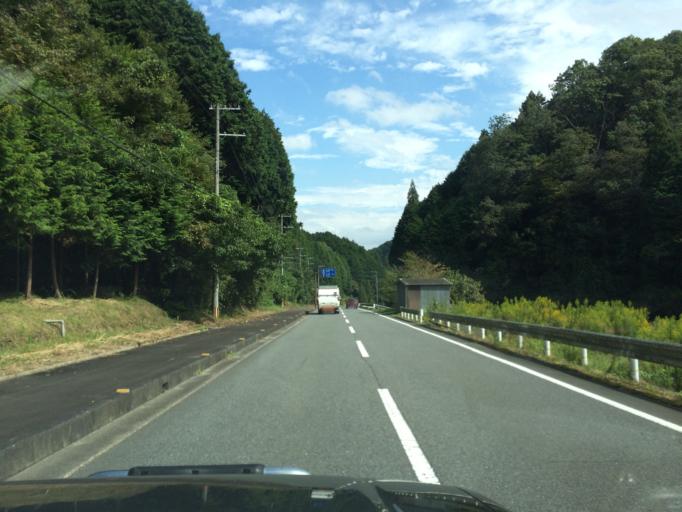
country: JP
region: Mie
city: Nabari
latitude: 34.6780
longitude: 136.0249
